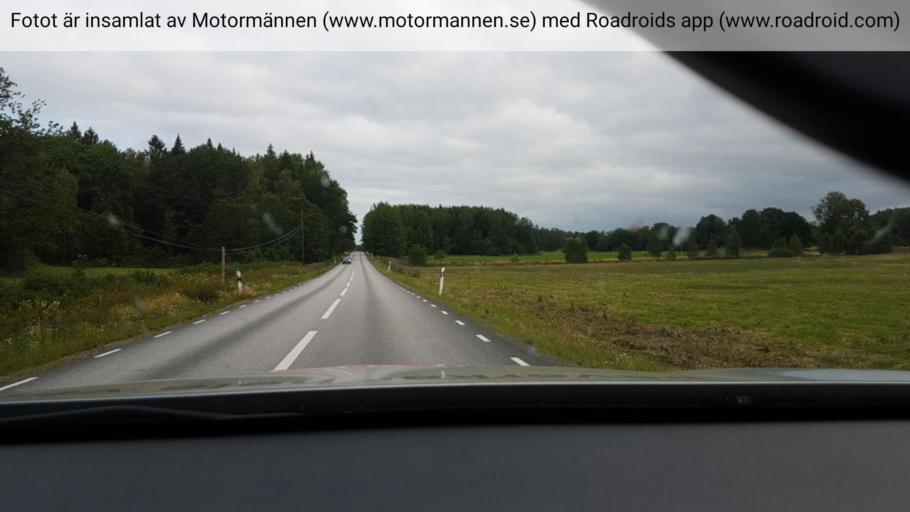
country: SE
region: Stockholm
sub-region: Norrtalje Kommun
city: Skanninge
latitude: 59.8310
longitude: 18.4426
